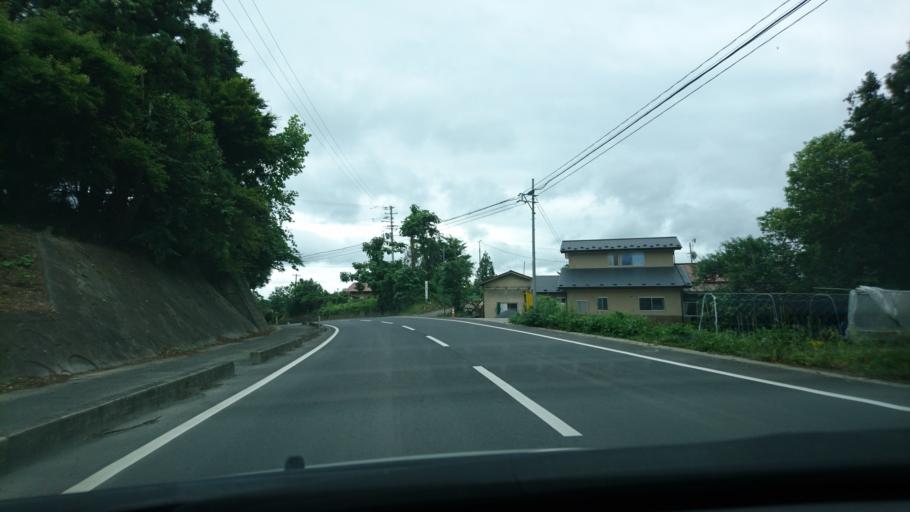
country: JP
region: Iwate
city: Ichinoseki
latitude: 38.7486
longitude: 141.2544
